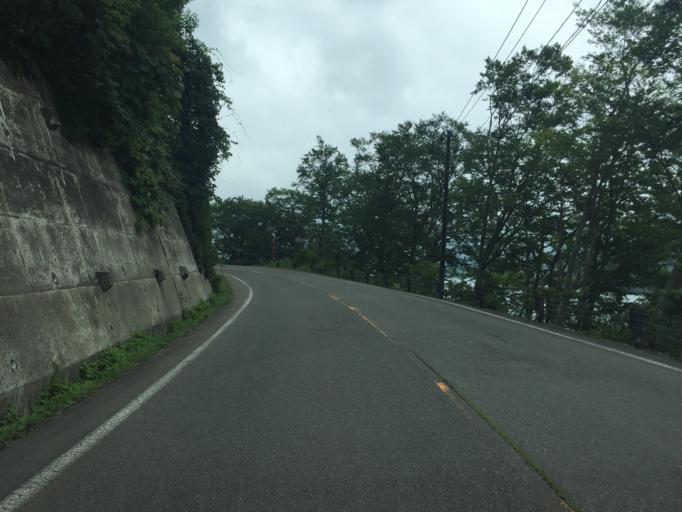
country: JP
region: Fukushima
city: Inawashiro
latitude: 37.6947
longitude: 140.0596
